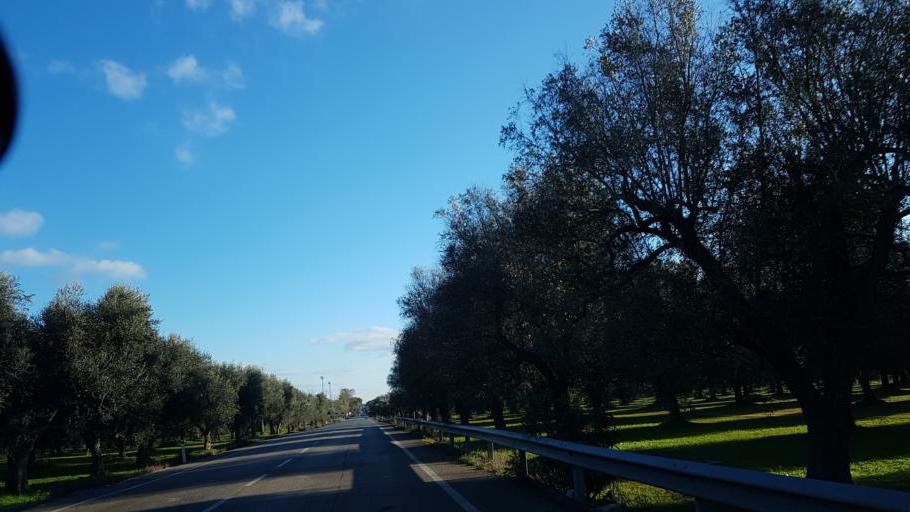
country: IT
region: Apulia
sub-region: Provincia di Lecce
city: Squinzano
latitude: 40.4487
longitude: 18.0299
